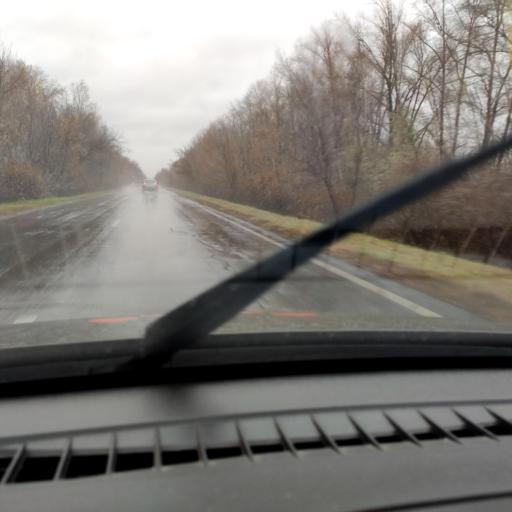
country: RU
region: Samara
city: Tol'yatti
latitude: 53.6854
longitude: 49.2563
